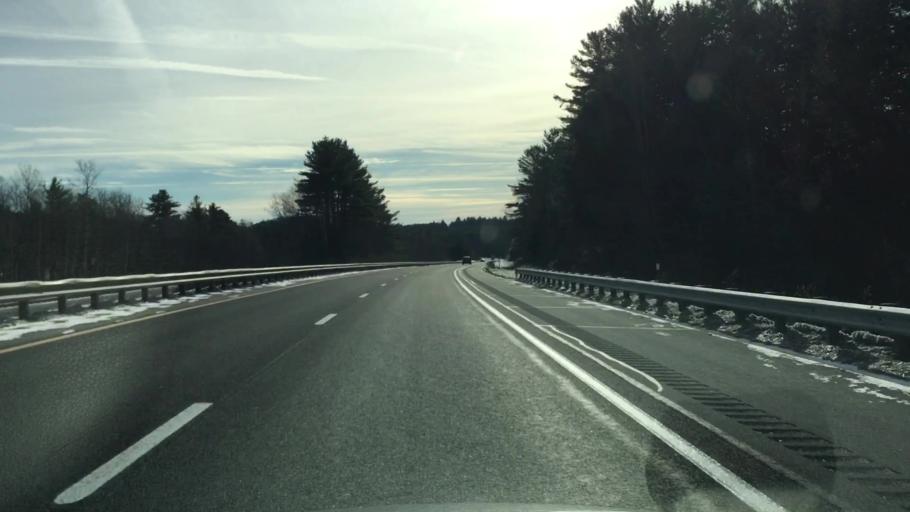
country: US
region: New Hampshire
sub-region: Sullivan County
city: Grantham
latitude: 43.5329
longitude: -72.1398
